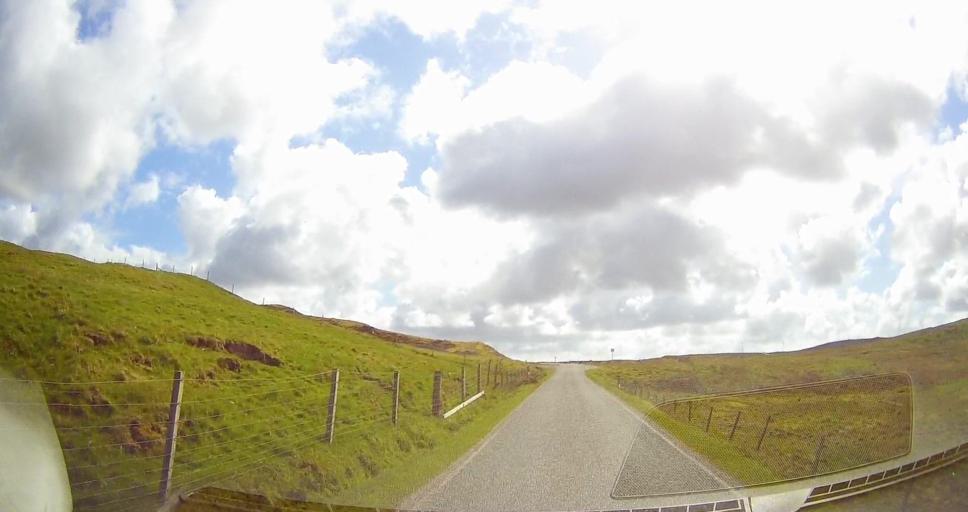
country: GB
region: Scotland
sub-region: Shetland Islands
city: Lerwick
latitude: 60.5226
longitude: -1.3750
